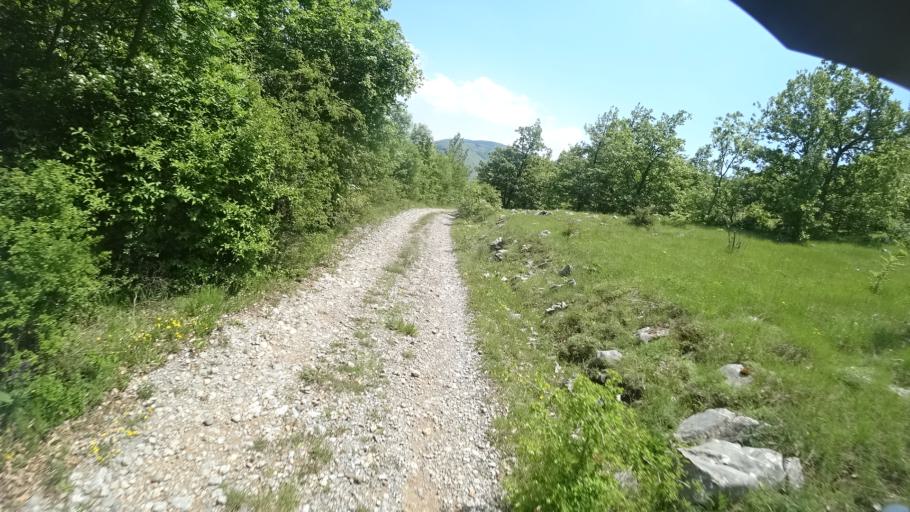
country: HR
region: Zadarska
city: Gracac
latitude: 44.4448
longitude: 15.9125
